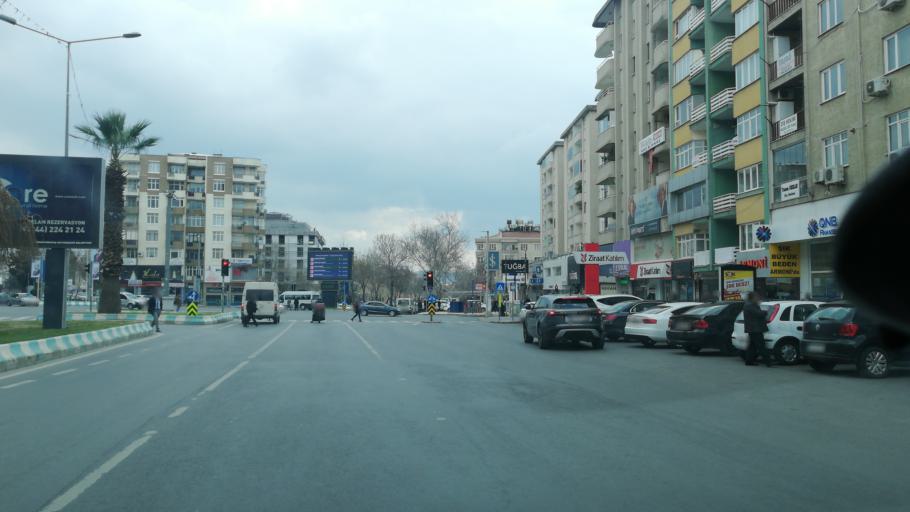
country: TR
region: Kahramanmaras
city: Kahramanmaras
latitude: 37.5753
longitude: 36.9326
